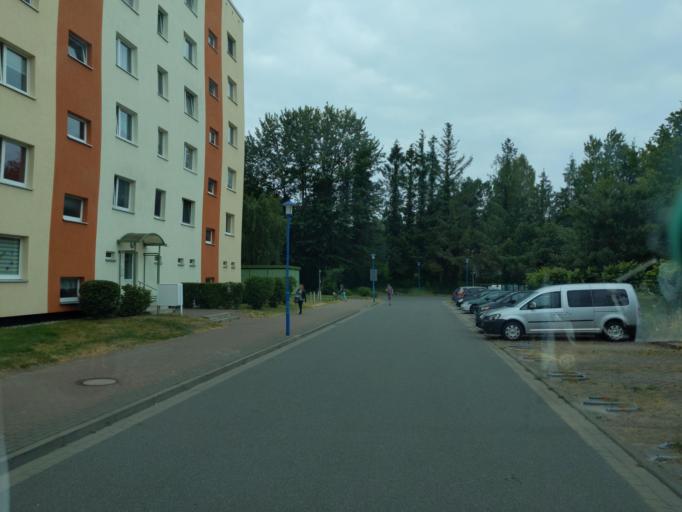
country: DE
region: Mecklenburg-Vorpommern
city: Seeheilbad Graal-Muritz
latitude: 54.2510
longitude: 12.2458
